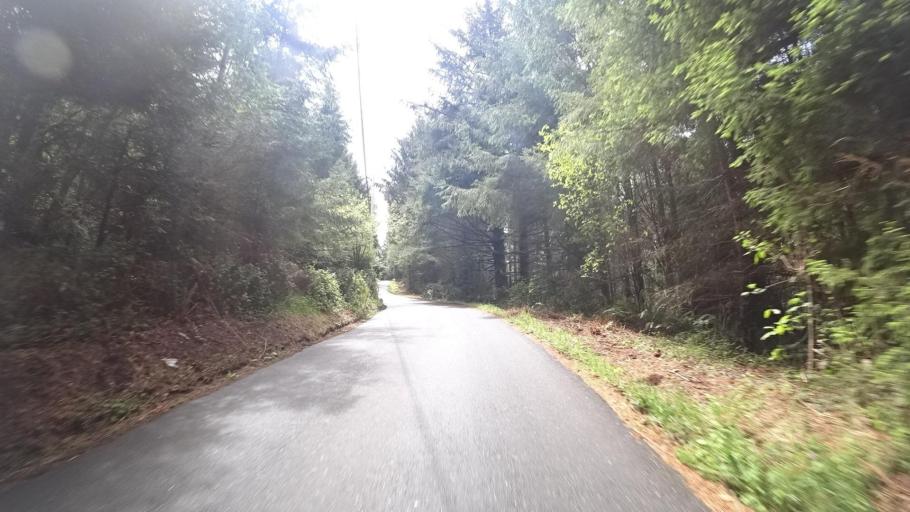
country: US
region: California
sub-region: Humboldt County
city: Bayside
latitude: 40.8334
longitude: -124.0136
